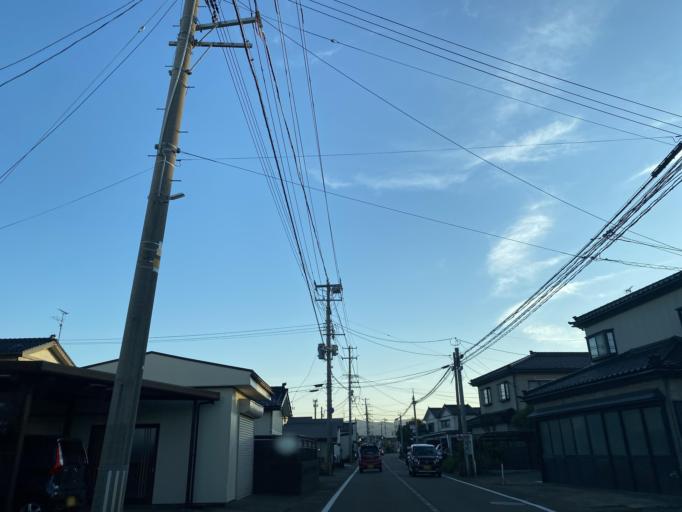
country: JP
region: Niigata
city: Kashiwazaki
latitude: 37.3816
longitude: 138.5680
